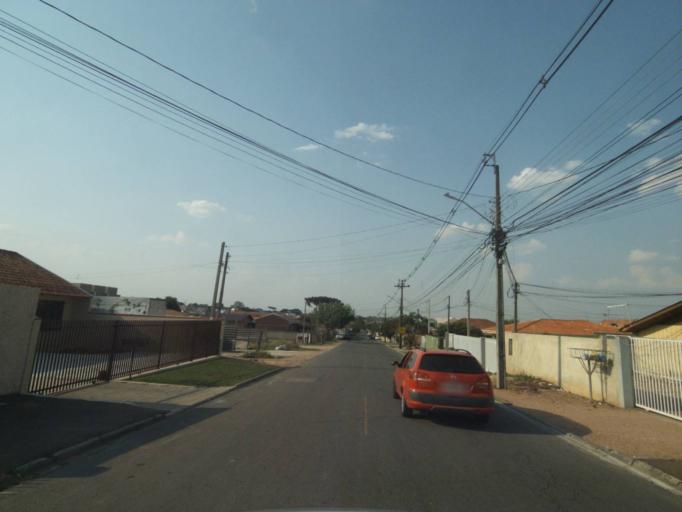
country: BR
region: Parana
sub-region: Sao Jose Dos Pinhais
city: Sao Jose dos Pinhais
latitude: -25.5315
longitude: -49.2369
